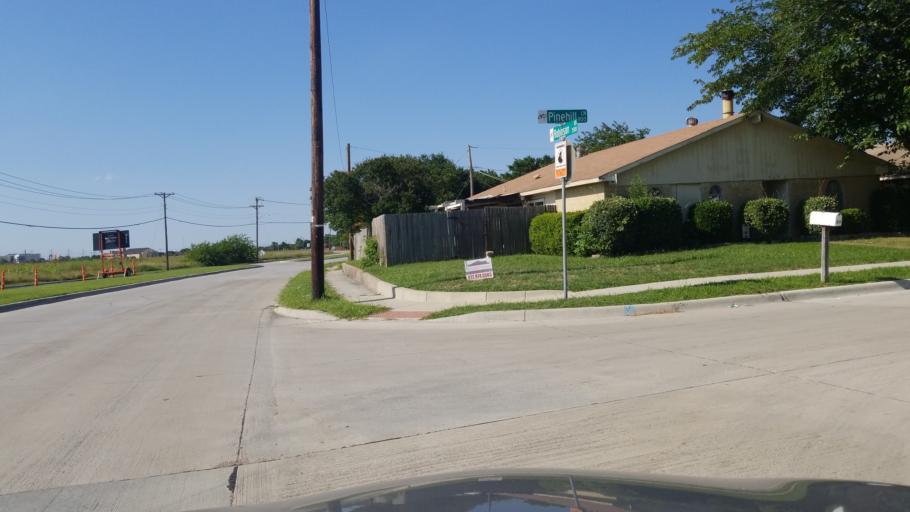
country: US
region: Texas
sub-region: Dallas County
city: Grand Prairie
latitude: 32.6841
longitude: -97.0190
